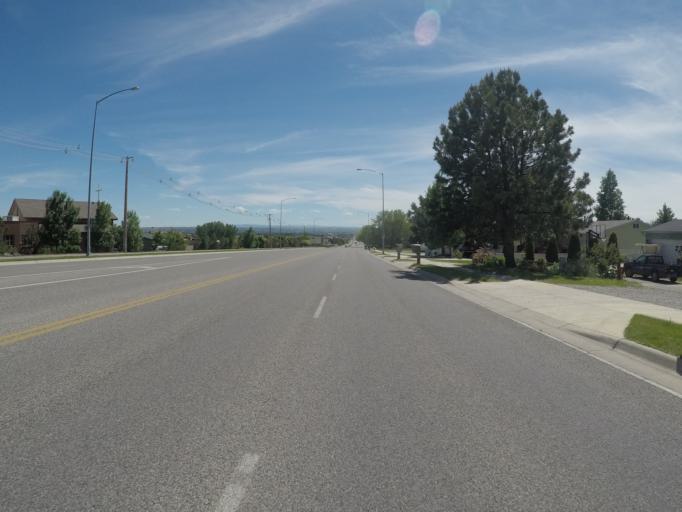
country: US
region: Montana
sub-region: Yellowstone County
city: Billings
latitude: 45.7947
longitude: -108.6177
